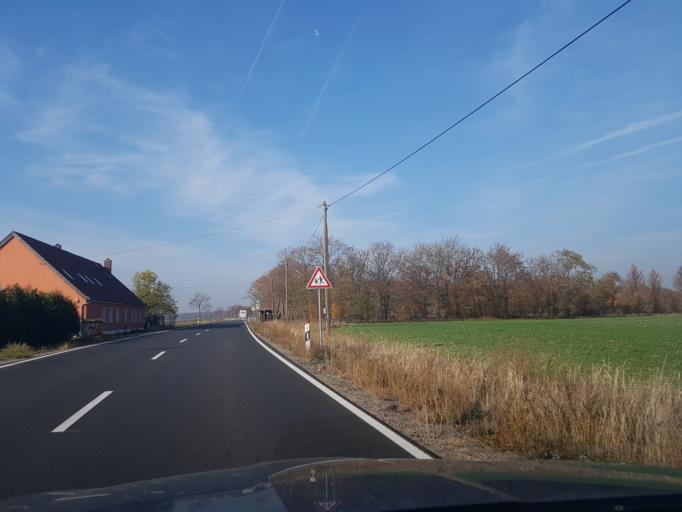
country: DE
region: Saxony
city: Arzberg
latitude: 51.5479
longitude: 13.1592
